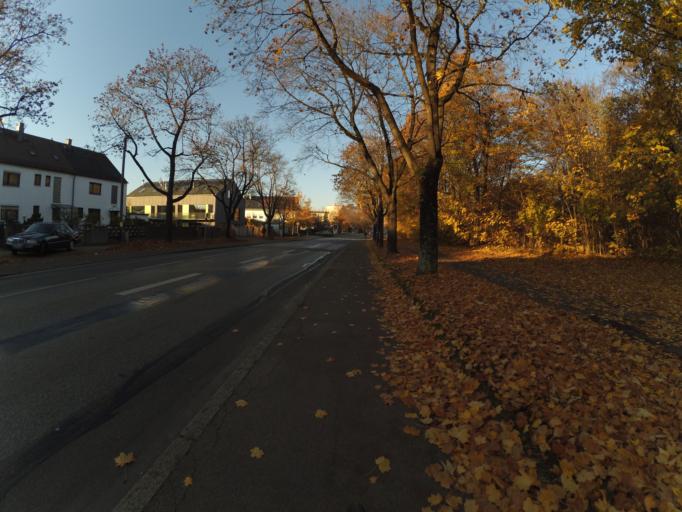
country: DE
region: Bavaria
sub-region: Upper Bavaria
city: Oberschleissheim
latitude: 48.1940
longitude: 11.5345
